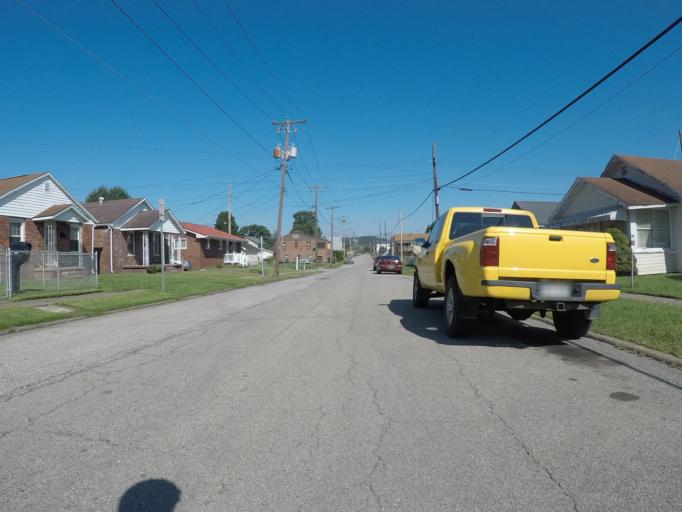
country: US
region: Ohio
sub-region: Lawrence County
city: Burlington
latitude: 38.4004
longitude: -82.5000
